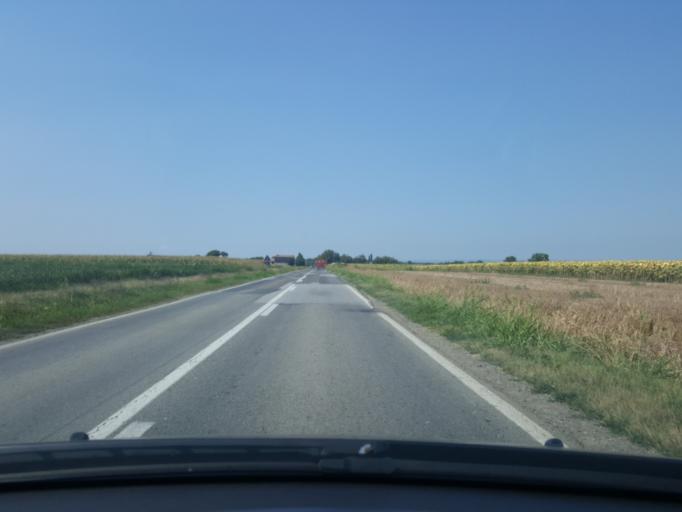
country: RS
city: Hrtkovci
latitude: 44.8629
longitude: 19.7717
